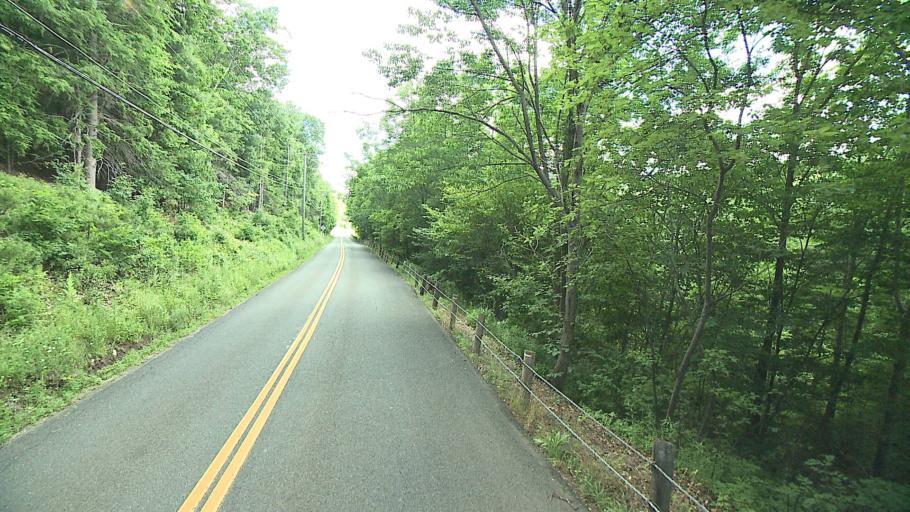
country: US
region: Connecticut
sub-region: Litchfield County
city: Litchfield
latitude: 41.8369
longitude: -73.3190
